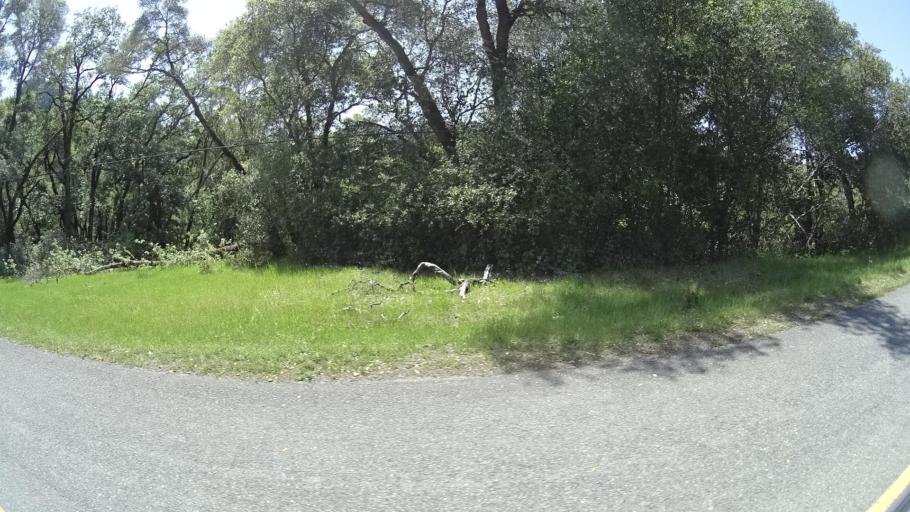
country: US
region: California
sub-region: Humboldt County
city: Redway
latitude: 40.2353
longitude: -123.6187
